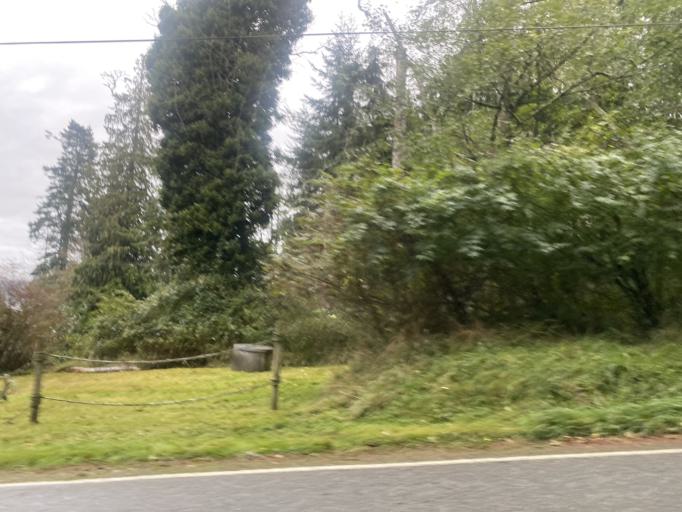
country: US
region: Washington
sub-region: Island County
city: Camano
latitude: 48.0953
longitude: -122.5092
